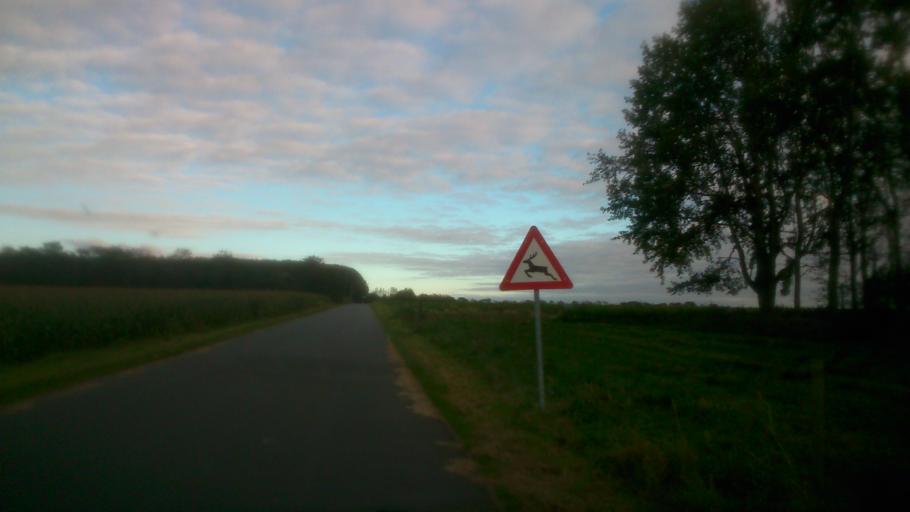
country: DK
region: Central Jutland
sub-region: Holstebro Kommune
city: Ulfborg
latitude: 56.1564
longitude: 8.4100
